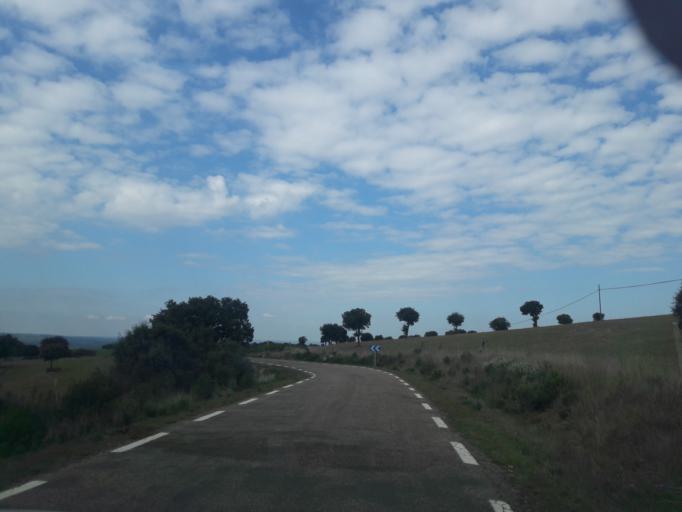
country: ES
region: Castille and Leon
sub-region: Provincia de Salamanca
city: Zamarra
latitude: 40.5438
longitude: -6.4095
